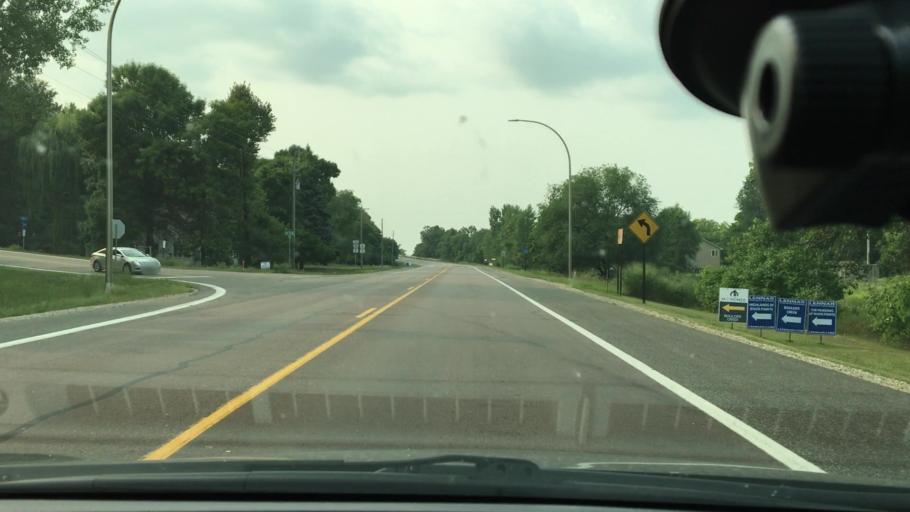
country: US
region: Minnesota
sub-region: Hennepin County
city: Dayton
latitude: 45.2519
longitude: -93.5375
